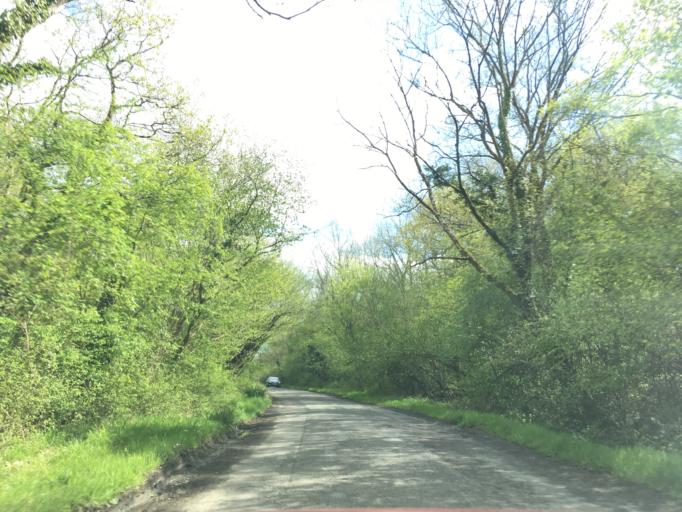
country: GB
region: England
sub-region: South Gloucestershire
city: Horton
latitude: 51.5931
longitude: -2.3585
